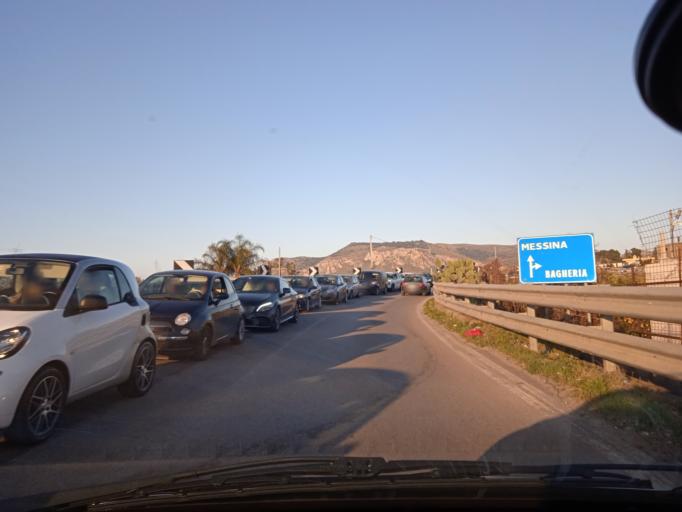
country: IT
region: Sicily
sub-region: Palermo
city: Ficarazzi
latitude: 38.0917
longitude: 13.4764
